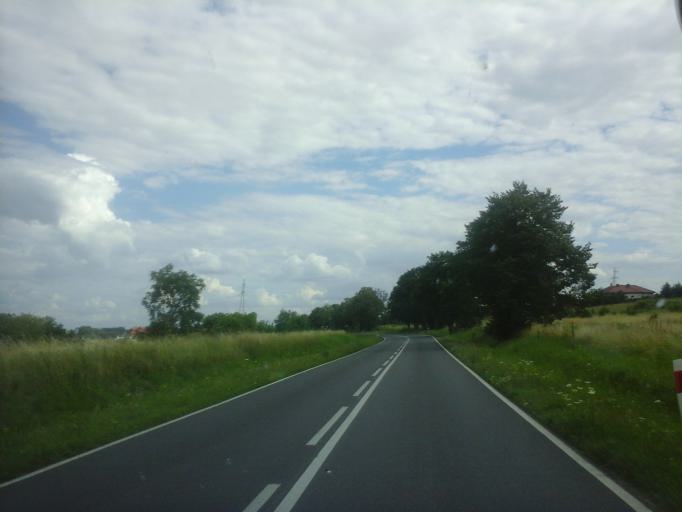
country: PL
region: West Pomeranian Voivodeship
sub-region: Powiat stargardzki
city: Stargard Szczecinski
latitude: 53.3650
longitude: 15.0034
